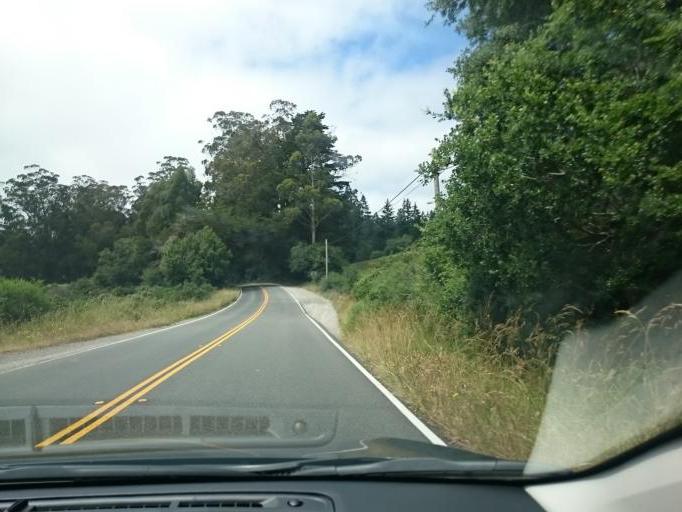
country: US
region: California
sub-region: Marin County
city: Lagunitas-Forest Knolls
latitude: 37.9683
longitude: -122.7256
